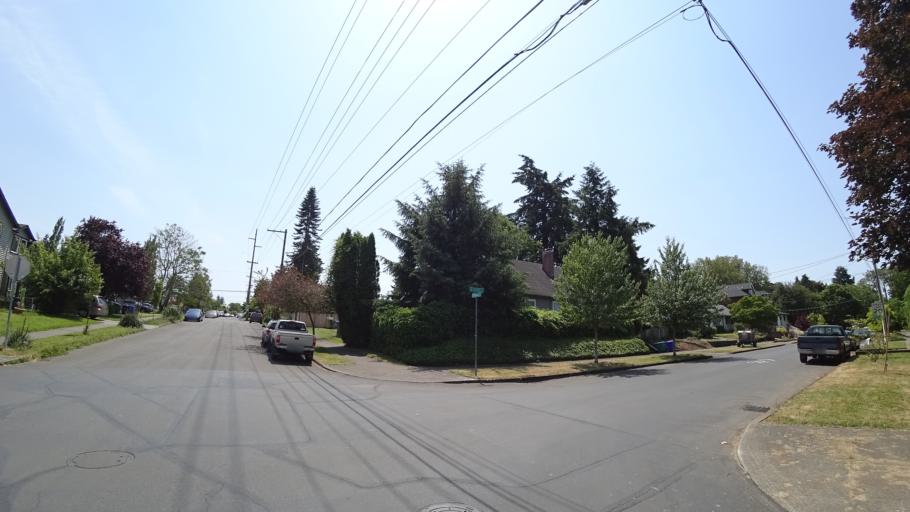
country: US
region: Oregon
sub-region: Multnomah County
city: Portland
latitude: 45.5799
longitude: -122.6925
